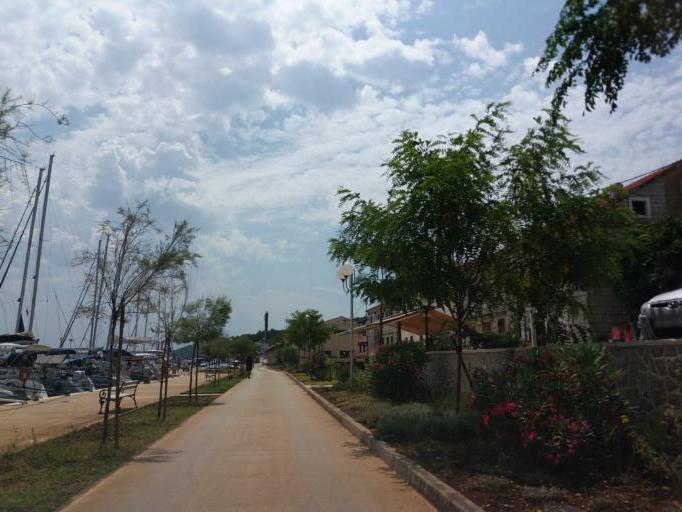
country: HR
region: Zadarska
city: Sali
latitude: 43.9360
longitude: 15.1664
